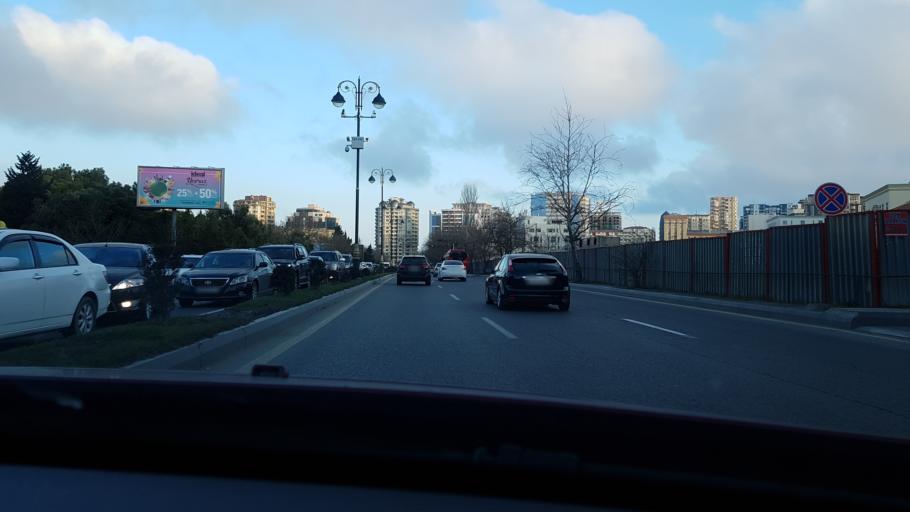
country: AZ
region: Baki
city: Badamdar
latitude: 40.3905
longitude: 49.8243
